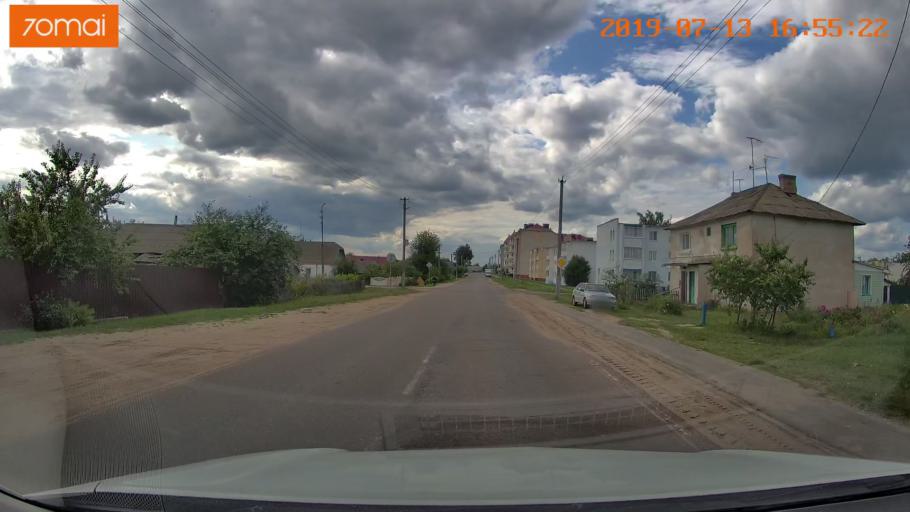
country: BY
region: Mogilev
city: Kirawsk
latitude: 53.2673
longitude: 29.4680
